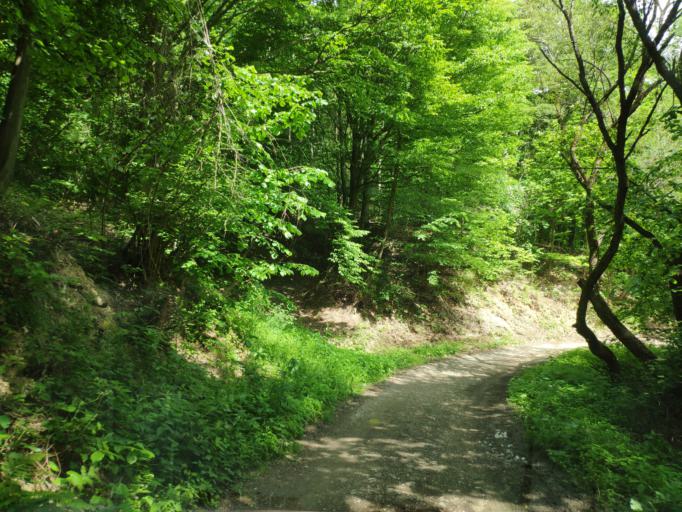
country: SK
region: Kosicky
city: Medzev
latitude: 48.7216
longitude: 20.9644
